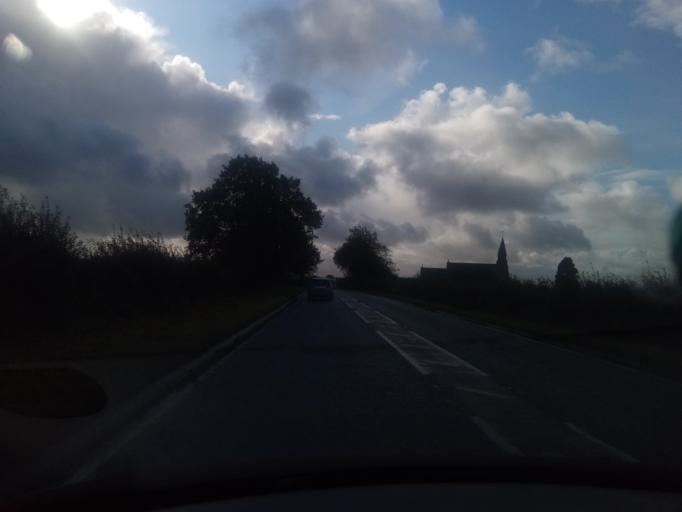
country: GB
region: England
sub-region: Cumbria
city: Carlisle
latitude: 54.9546
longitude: -2.9439
